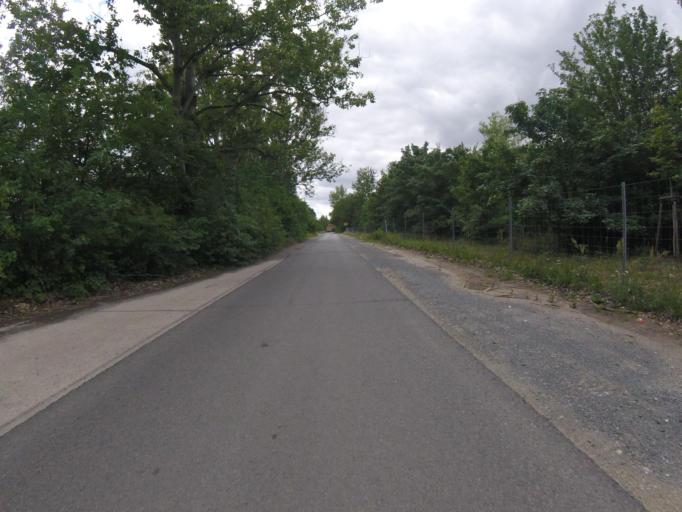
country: DE
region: Brandenburg
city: Konigs Wusterhausen
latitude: 52.3041
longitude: 13.6642
